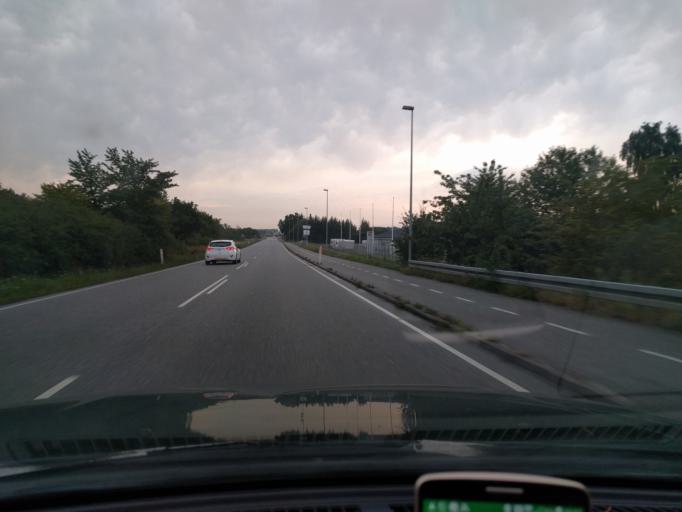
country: DK
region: Zealand
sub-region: Guldborgsund Kommune
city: Norre Alslev
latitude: 54.9502
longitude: 11.8661
